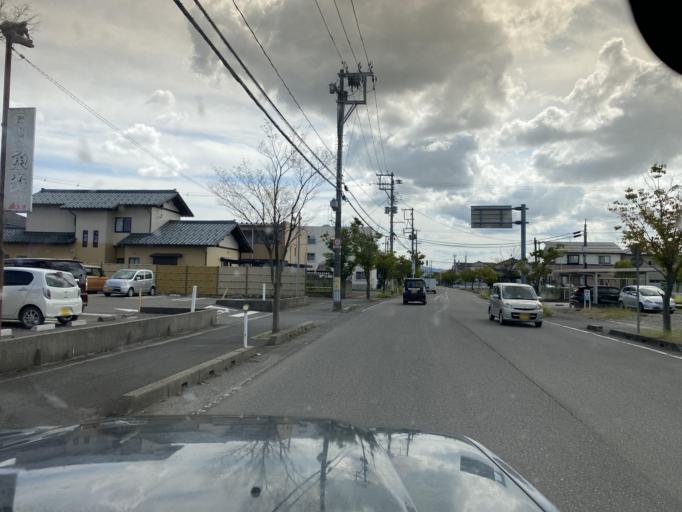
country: JP
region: Niigata
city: Niitsu-honcho
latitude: 37.8140
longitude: 139.1162
